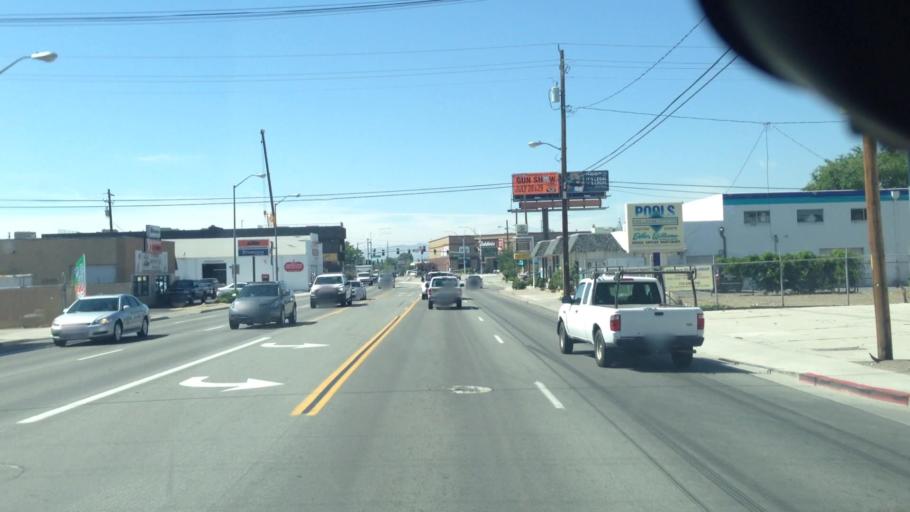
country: US
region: Nevada
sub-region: Washoe County
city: Sparks
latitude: 39.5298
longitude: -119.7664
